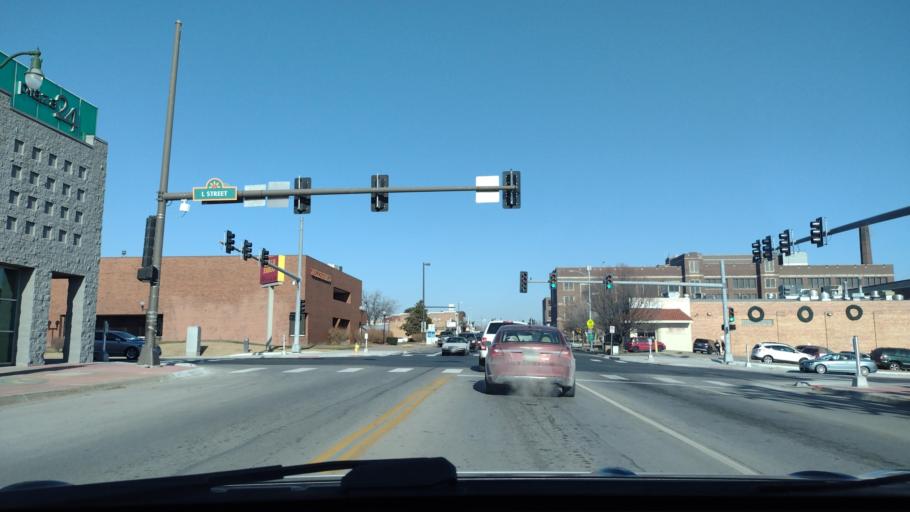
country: US
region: Nebraska
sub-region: Douglas County
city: Omaha
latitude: 41.2120
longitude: -95.9470
